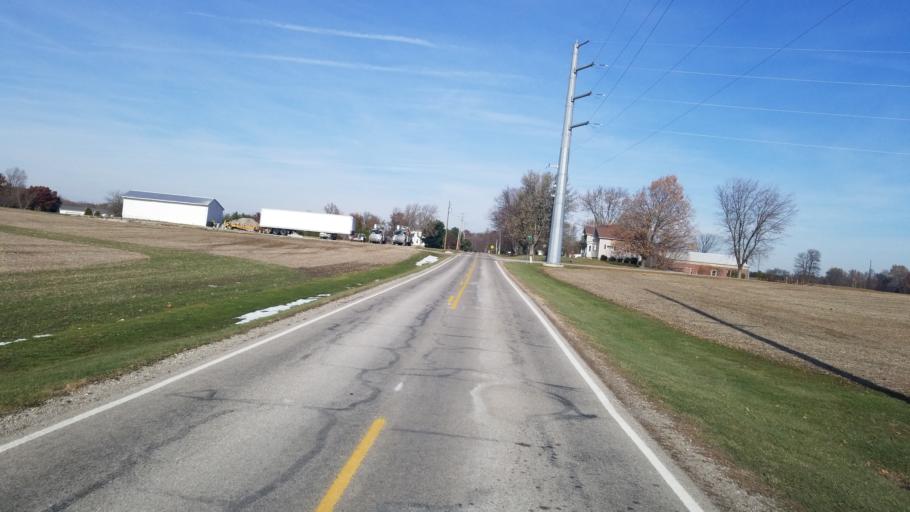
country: US
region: Ohio
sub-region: Huron County
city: Monroeville
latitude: 41.1850
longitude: -82.6817
